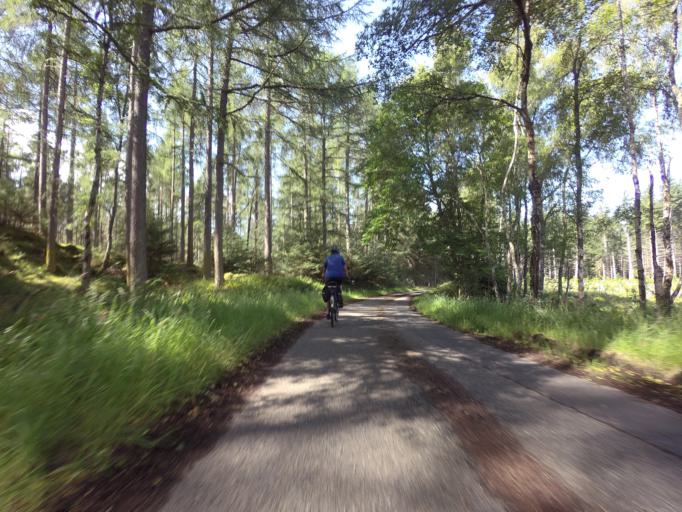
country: GB
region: Scotland
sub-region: Highland
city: Nairn
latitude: 57.5017
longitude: -3.9261
